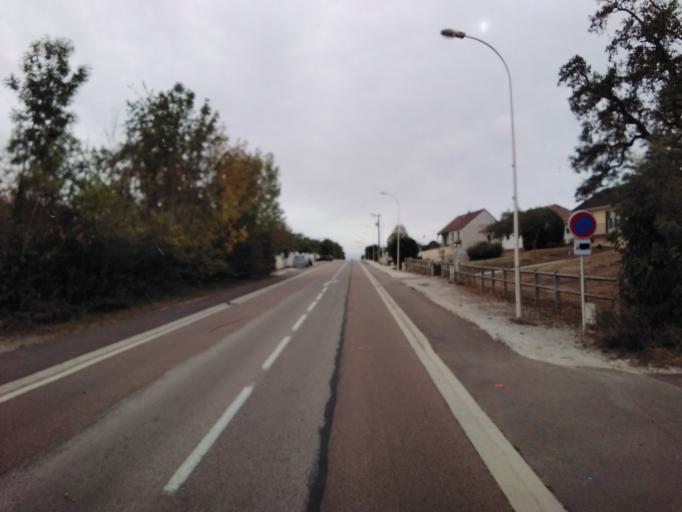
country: FR
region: Champagne-Ardenne
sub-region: Departement de l'Aube
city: Vendeuvre-sur-Barse
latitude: 48.2329
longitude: 4.4622
